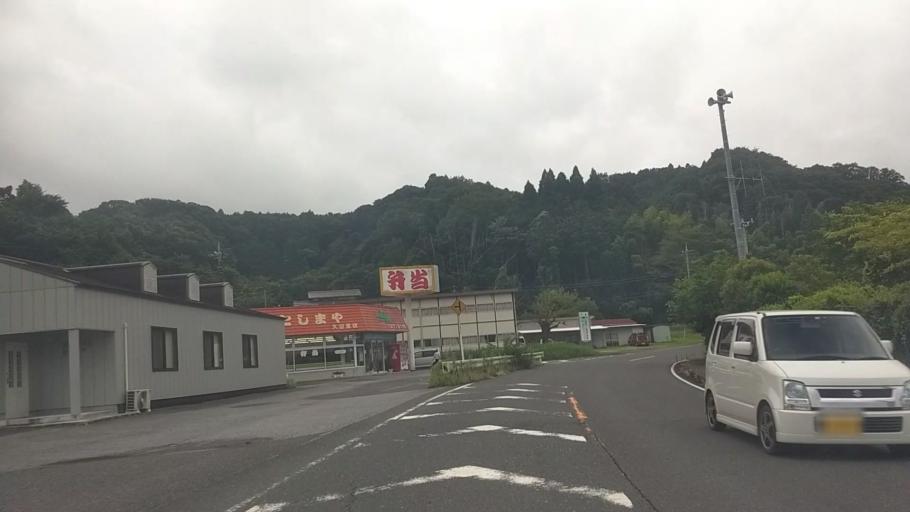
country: JP
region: Chiba
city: Kisarazu
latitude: 35.2865
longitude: 140.0831
